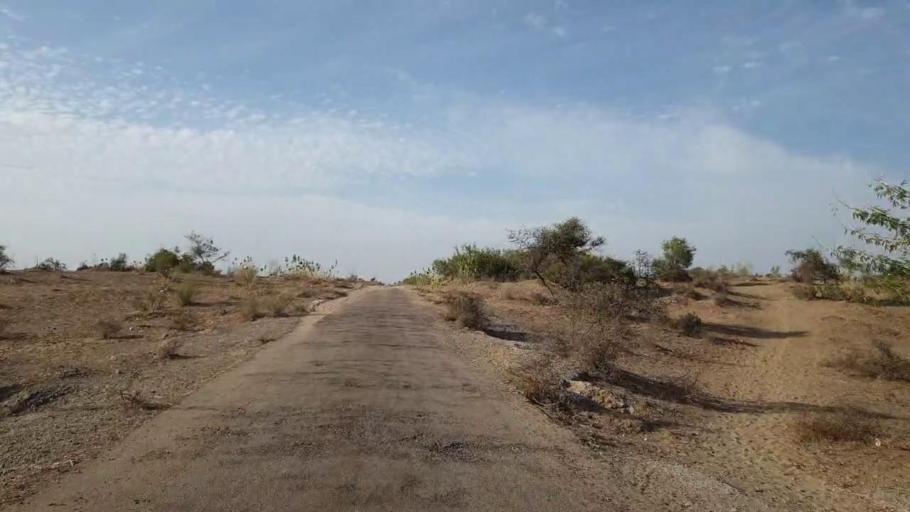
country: PK
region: Sindh
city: Nabisar
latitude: 25.0000
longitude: 69.9252
